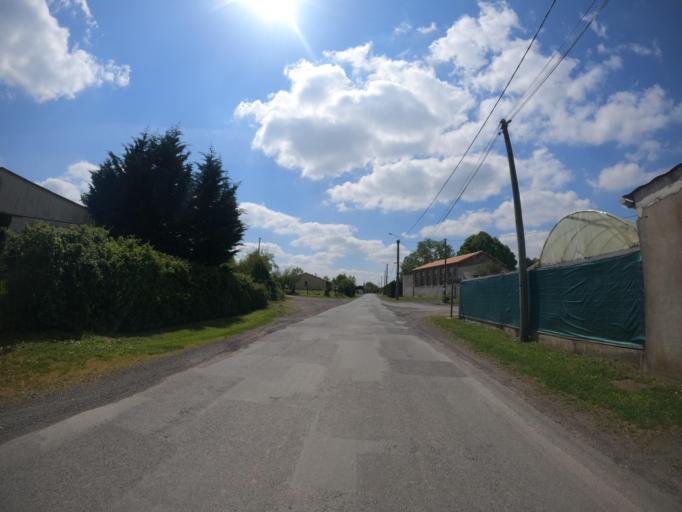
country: FR
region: Poitou-Charentes
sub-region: Departement des Deux-Sevres
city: Chiche
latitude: 46.8085
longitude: -0.2762
